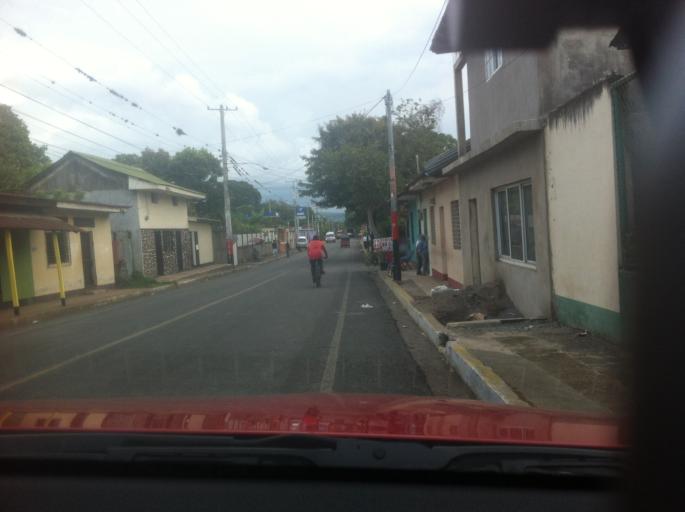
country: NI
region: Masaya
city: Masatepe
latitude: 11.9092
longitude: -86.1453
